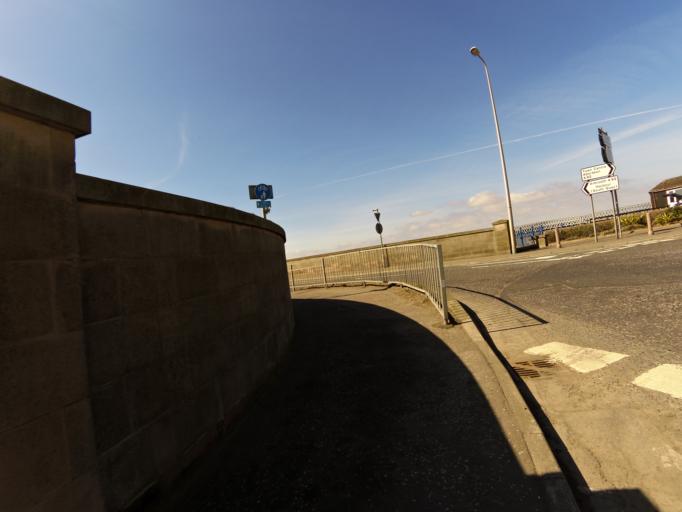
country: GB
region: Scotland
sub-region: Angus
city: Montrose
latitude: 56.7067
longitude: -2.4746
